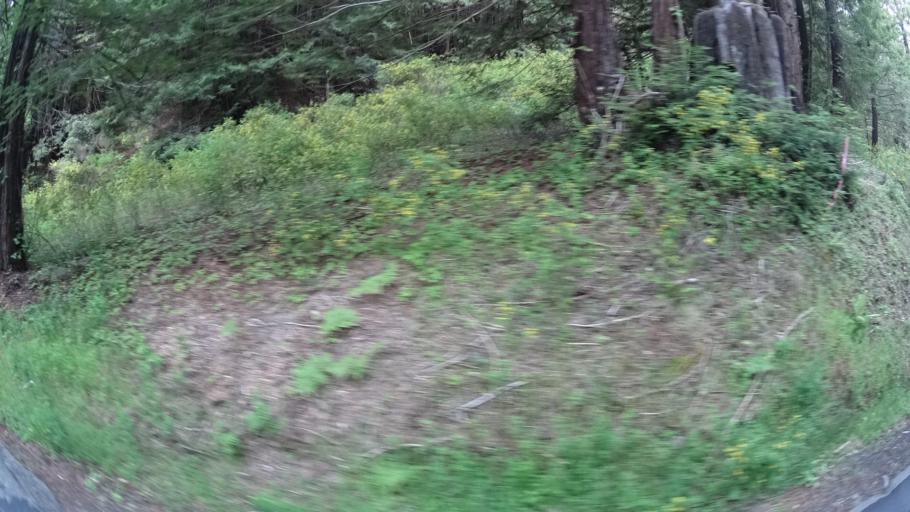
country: US
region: California
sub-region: Humboldt County
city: Redway
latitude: 40.2461
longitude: -123.8330
